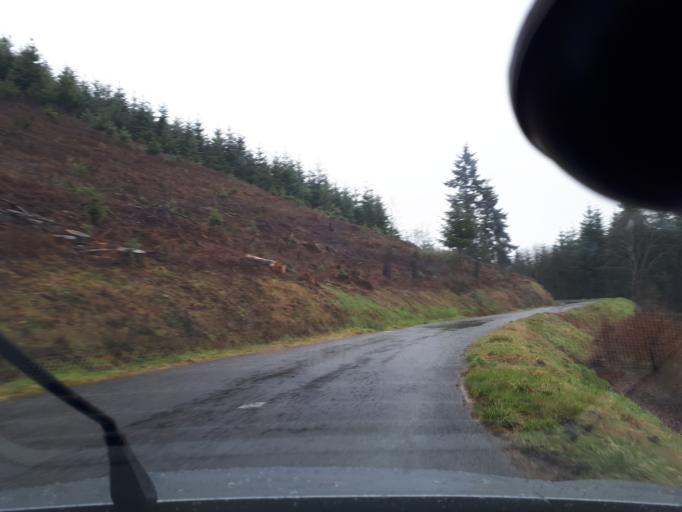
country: FR
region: Rhone-Alpes
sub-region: Departement du Rhone
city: Tarare
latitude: 45.9378
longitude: 4.4192
